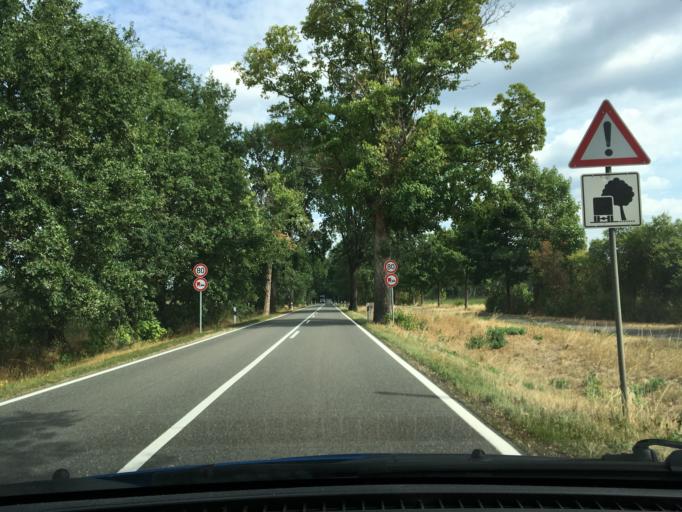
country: DE
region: Mecklenburg-Vorpommern
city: Eldena
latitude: 53.2652
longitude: 11.4514
